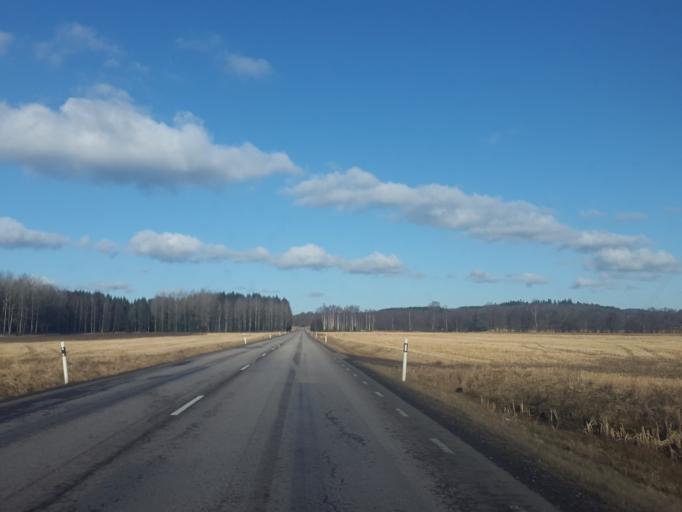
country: SE
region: Vaestra Goetaland
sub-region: Lerums Kommun
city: Grabo
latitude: 57.9089
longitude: 12.3402
